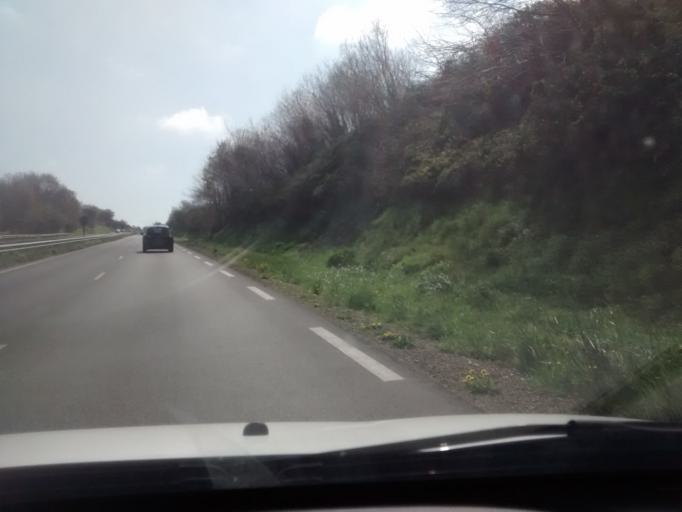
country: FR
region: Brittany
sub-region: Departement des Cotes-d'Armor
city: Saint-Quay-Perros
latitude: 48.7949
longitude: -3.4418
